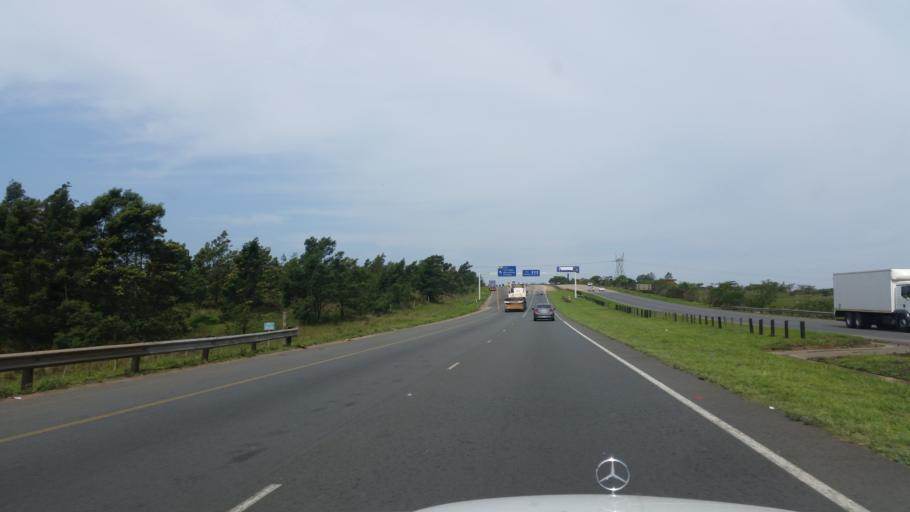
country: ZA
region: KwaZulu-Natal
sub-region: uMgungundlovu District Municipality
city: Camperdown
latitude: -29.7330
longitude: 30.5729
